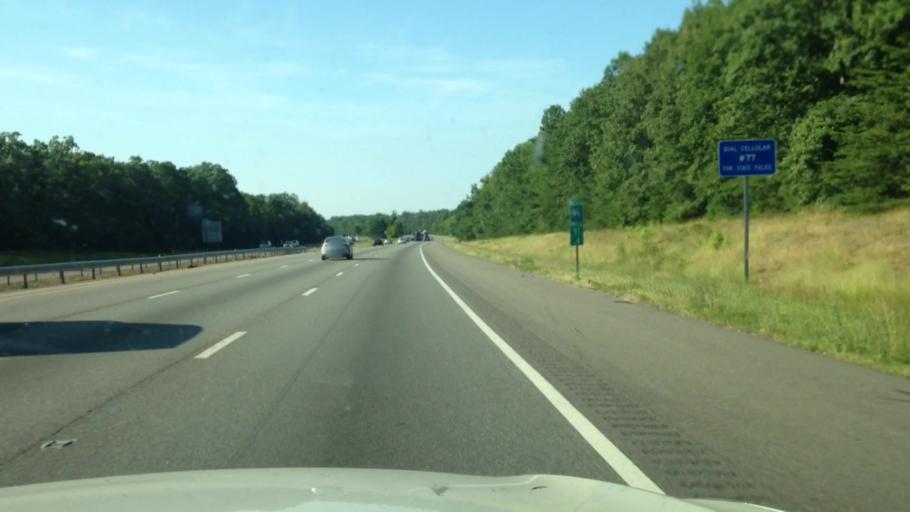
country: US
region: Virginia
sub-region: Hanover County
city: Ashland
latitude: 37.7784
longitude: -77.4614
